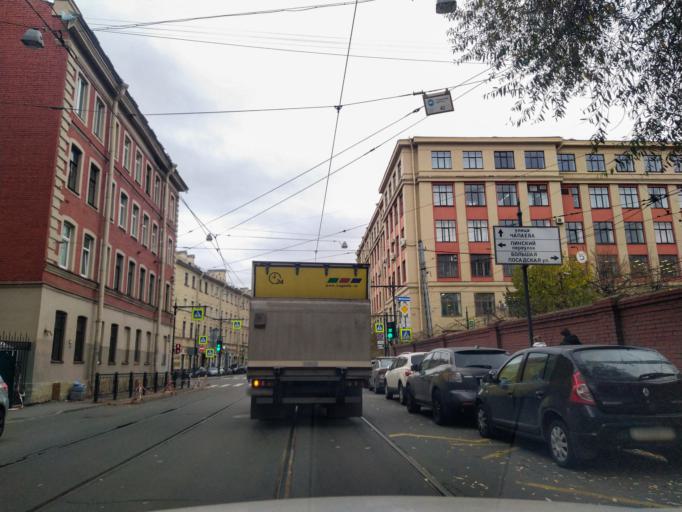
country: RU
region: St.-Petersburg
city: Petrogradka
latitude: 59.9610
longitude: 30.3304
